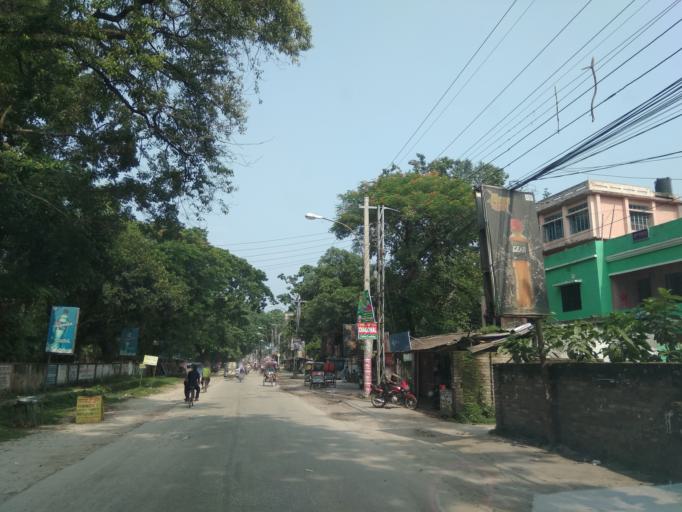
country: BD
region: Rangpur Division
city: Rangpur
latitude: 25.7582
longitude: 89.2357
